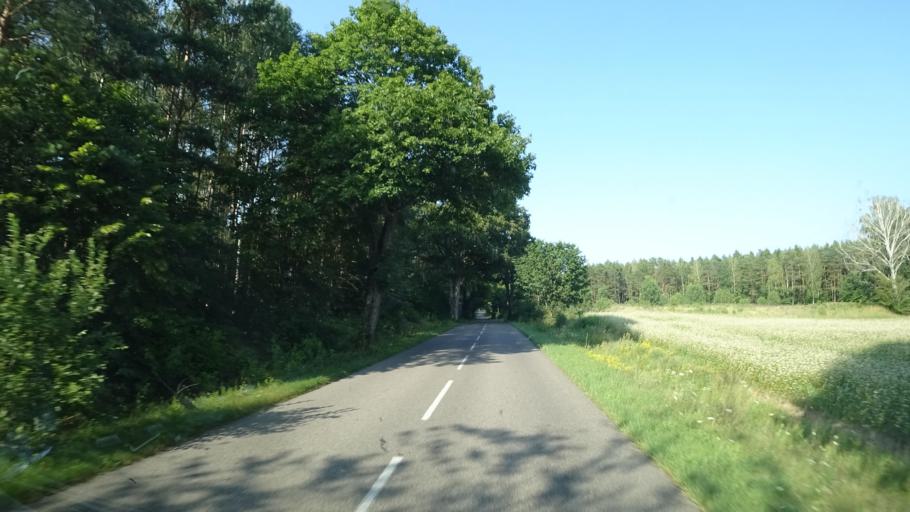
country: PL
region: Pomeranian Voivodeship
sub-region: Powiat czluchowski
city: Rzeczenica
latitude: 53.7654
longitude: 17.1414
